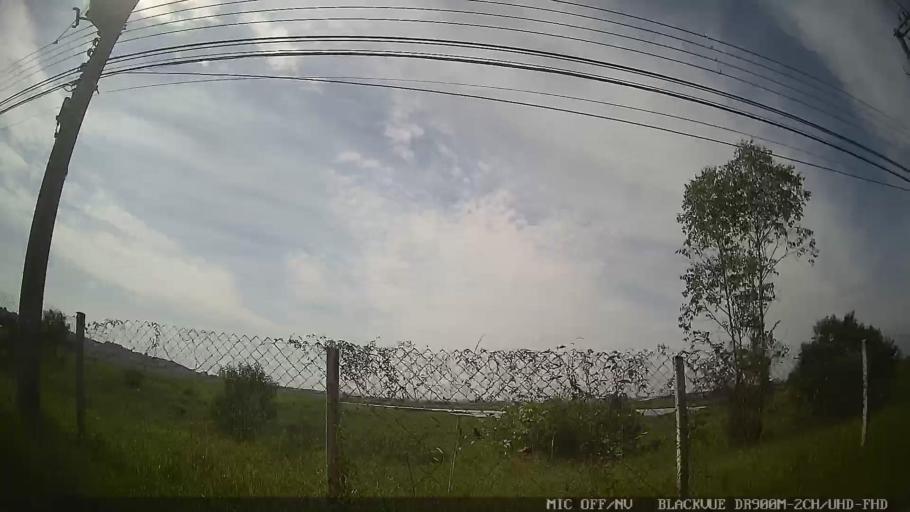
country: BR
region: Sao Paulo
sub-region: Itaquaquecetuba
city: Itaquaquecetuba
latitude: -23.4971
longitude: -46.3290
